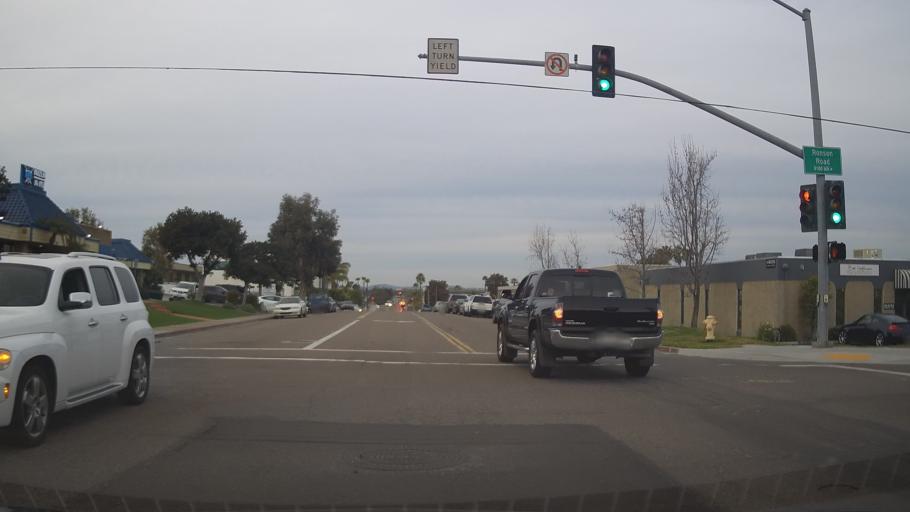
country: US
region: California
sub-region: San Diego County
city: San Diego
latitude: 32.8291
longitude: -117.1488
